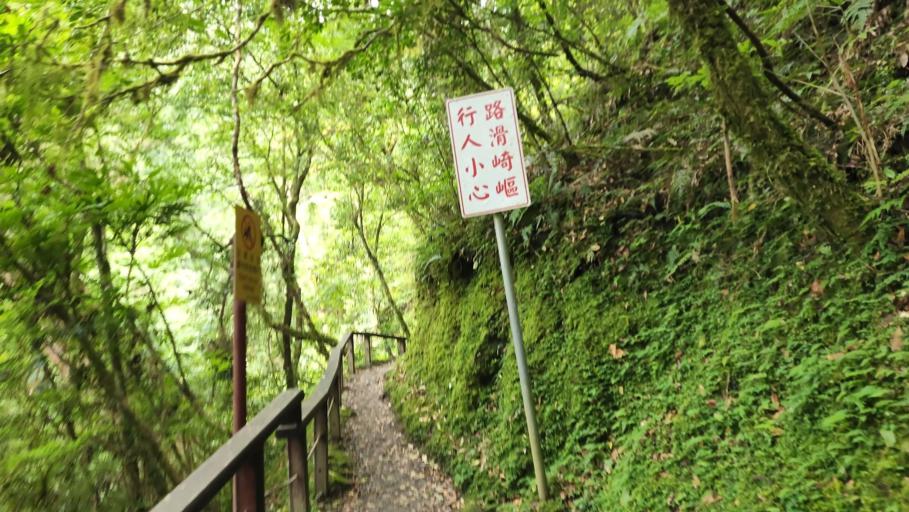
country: TW
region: Taiwan
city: Daxi
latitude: 24.7092
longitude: 121.4406
